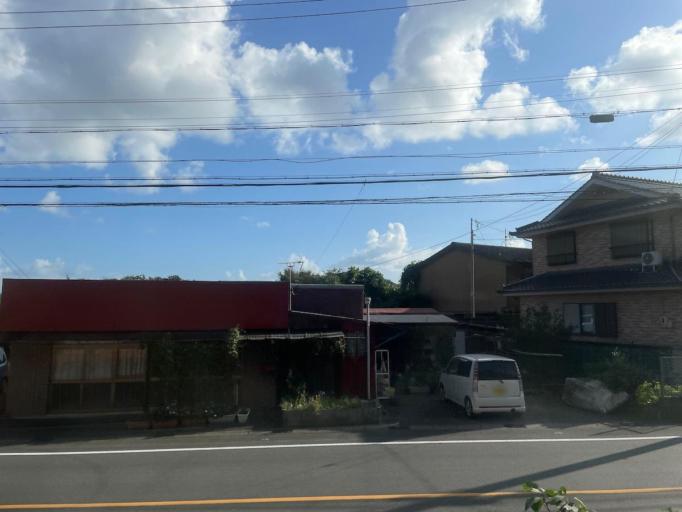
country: JP
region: Mie
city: Toba
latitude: 34.4621
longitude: 136.8411
